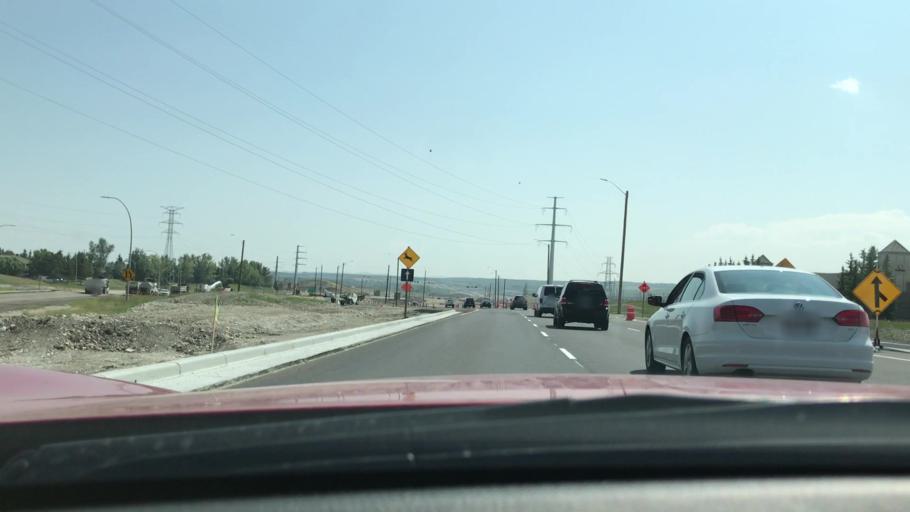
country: CA
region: Alberta
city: Calgary
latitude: 51.0163
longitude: -114.1661
